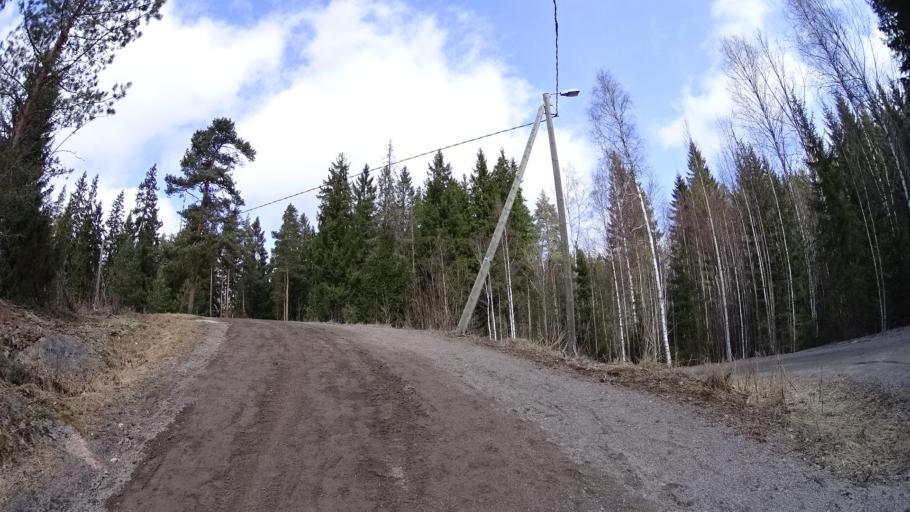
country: FI
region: Uusimaa
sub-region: Helsinki
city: Kilo
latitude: 60.2945
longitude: 24.8212
